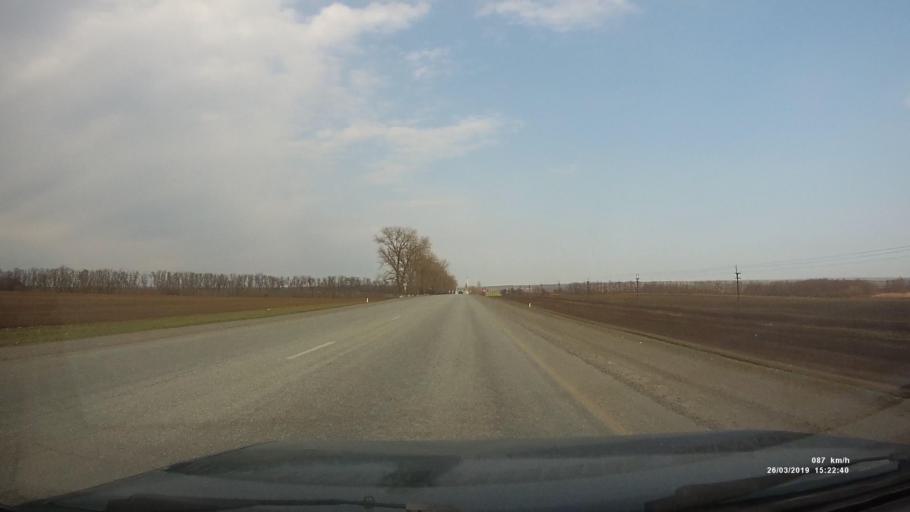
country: RU
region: Rostov
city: Primorka
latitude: 47.3082
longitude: 39.0006
